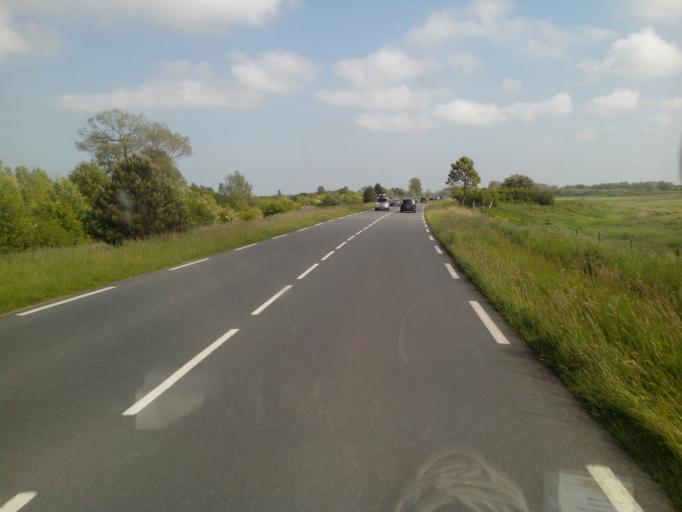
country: FR
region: Picardie
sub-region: Departement de la Somme
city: Saint-Valery-sur-Somme
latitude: 50.2053
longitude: 1.6828
